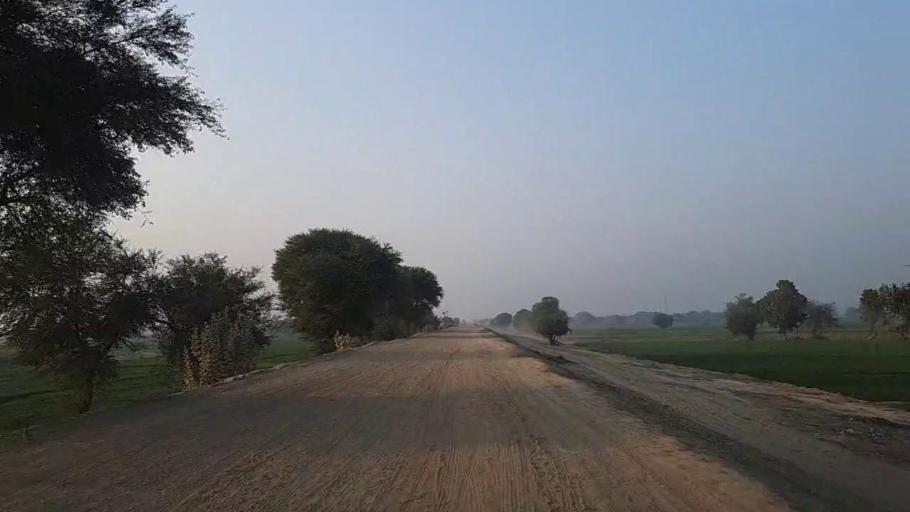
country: PK
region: Sindh
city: Sann
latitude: 26.1819
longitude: 68.0948
